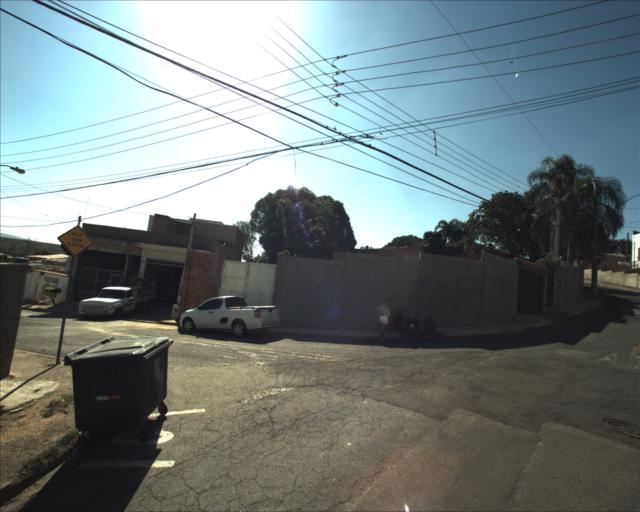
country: BR
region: Sao Paulo
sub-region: Sorocaba
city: Sorocaba
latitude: -23.4744
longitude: -47.5063
